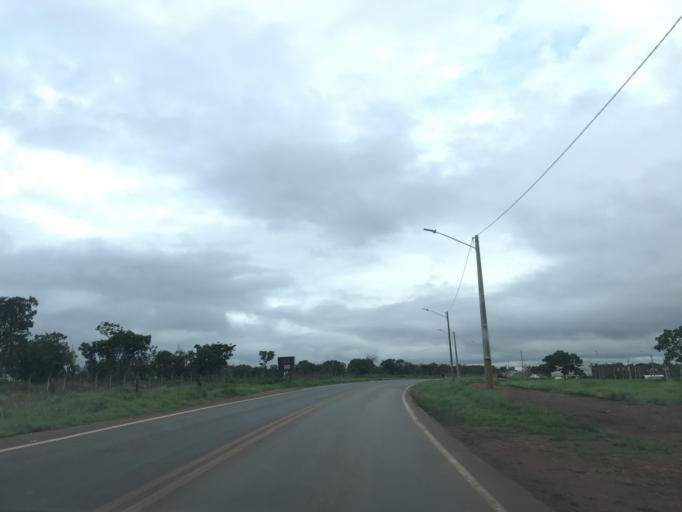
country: BR
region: Goias
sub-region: Luziania
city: Luziania
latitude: -16.2631
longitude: -47.9732
